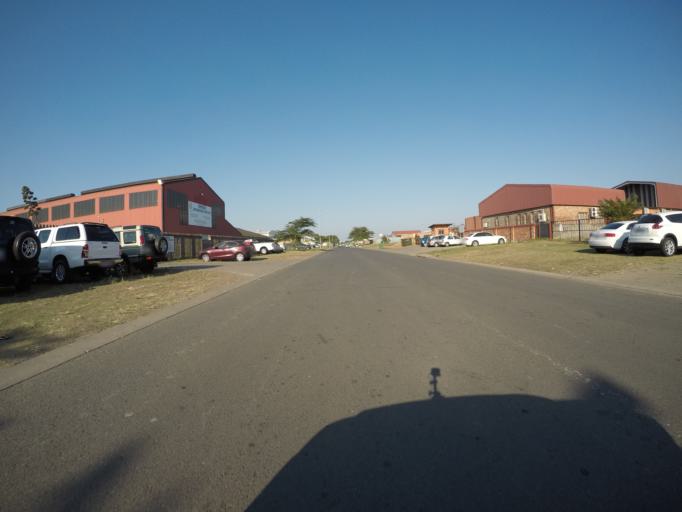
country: ZA
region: KwaZulu-Natal
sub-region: uThungulu District Municipality
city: Richards Bay
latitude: -28.7383
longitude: 32.0390
